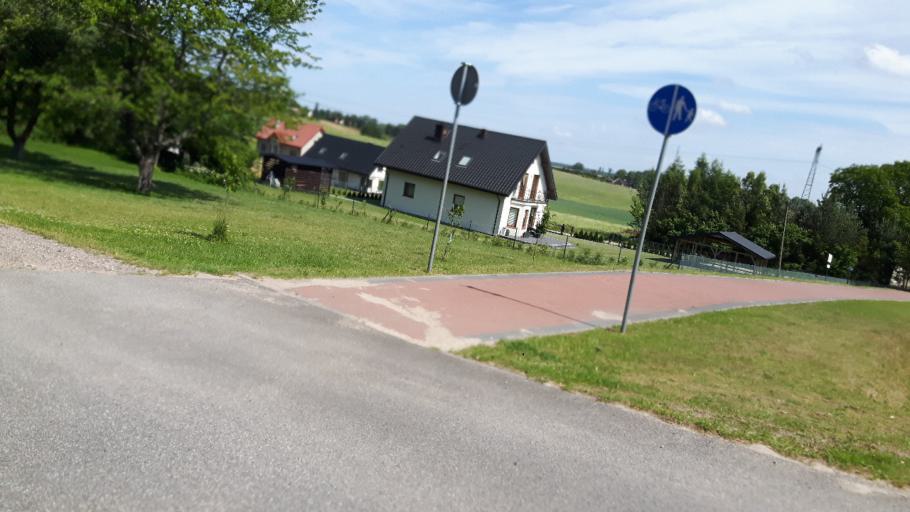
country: PL
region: Pomeranian Voivodeship
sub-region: Powiat wejherowski
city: Gniewino
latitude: 54.6906
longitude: 18.0754
